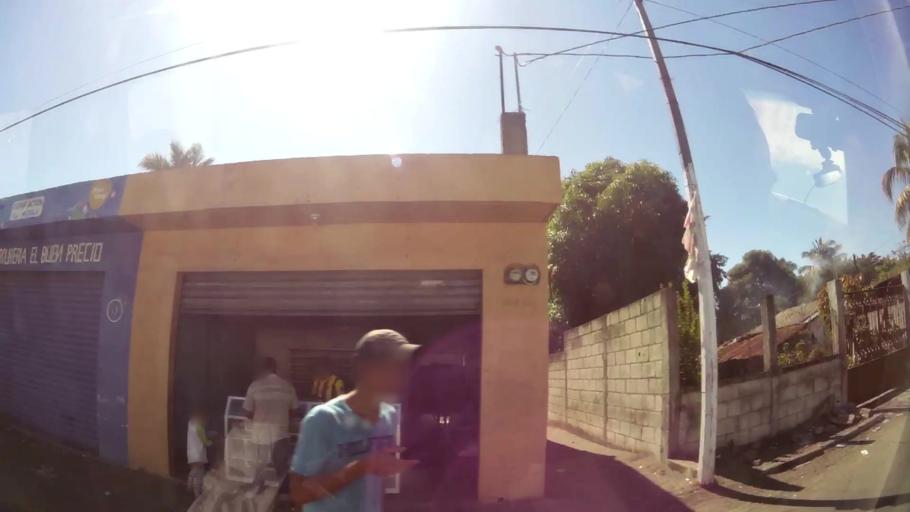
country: GT
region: Escuintla
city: Iztapa
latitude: 13.9321
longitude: -90.7057
